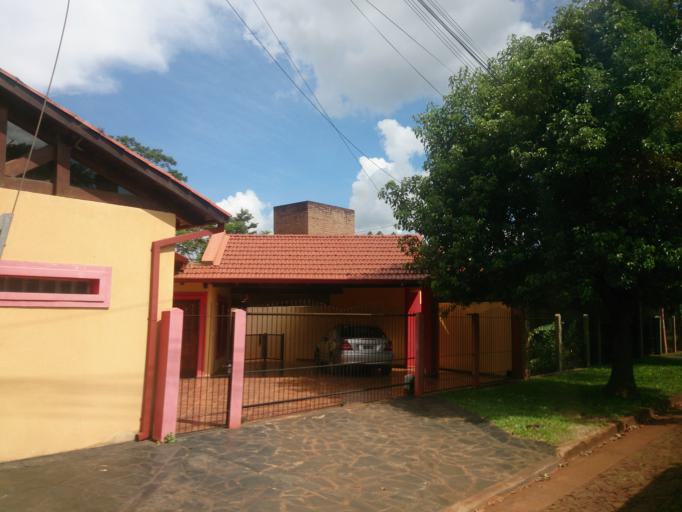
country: AR
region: Misiones
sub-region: Departamento de Obera
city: Obera
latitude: -27.4922
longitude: -55.1047
